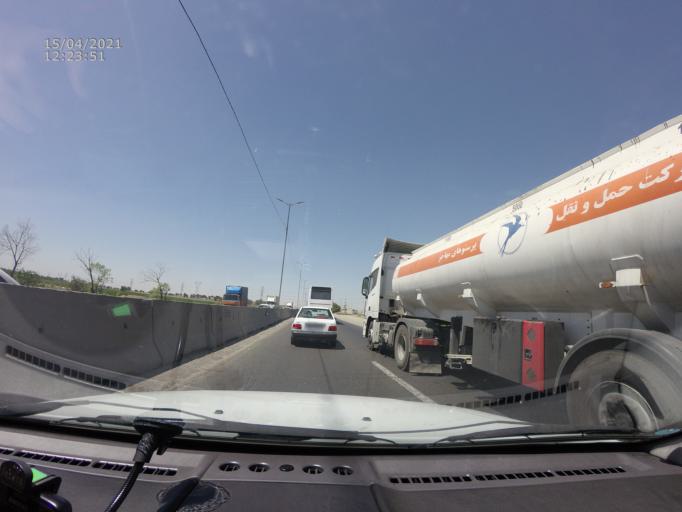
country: IR
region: Tehran
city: Eslamshahr
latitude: 35.5109
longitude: 51.2666
